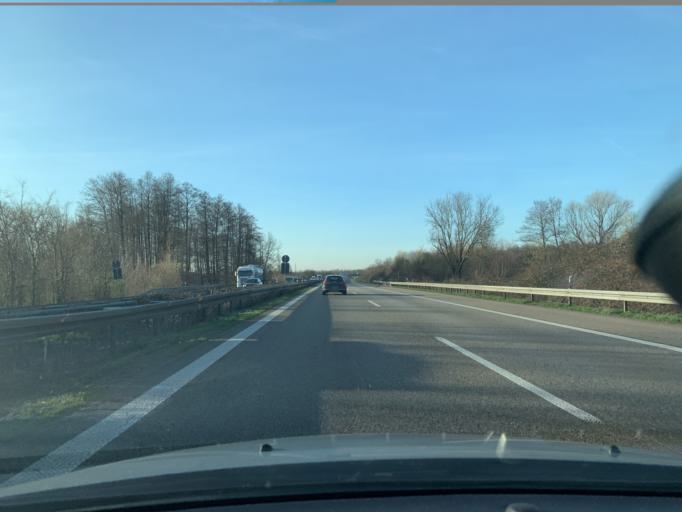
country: DE
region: Baden-Wuerttemberg
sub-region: Freiburg Region
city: Teningen
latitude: 48.0819
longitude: 7.8024
